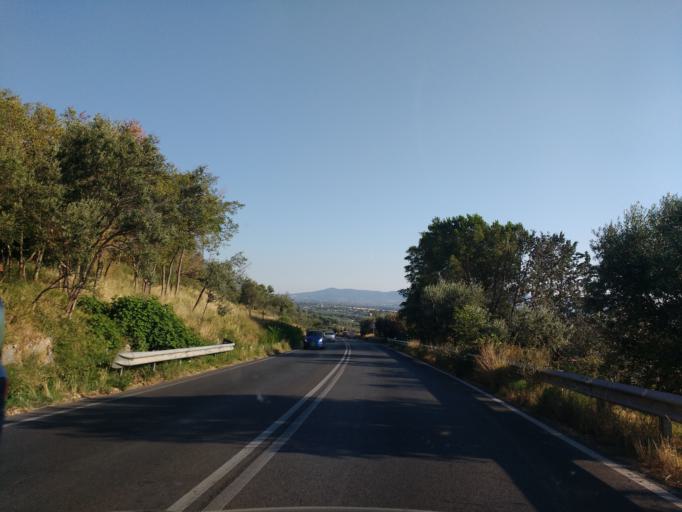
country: IT
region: Latium
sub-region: Citta metropolitana di Roma Capitale
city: Tivoli
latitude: 41.9519
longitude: 12.7910
